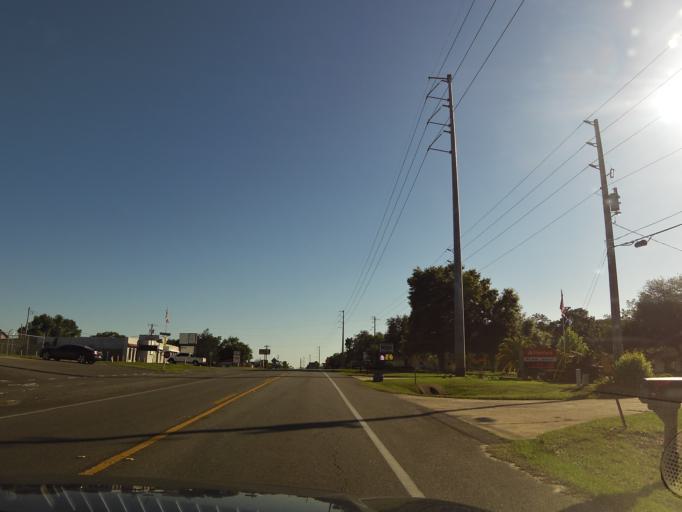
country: US
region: Florida
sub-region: Clay County
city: Keystone Heights
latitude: 29.7934
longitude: -82.0252
